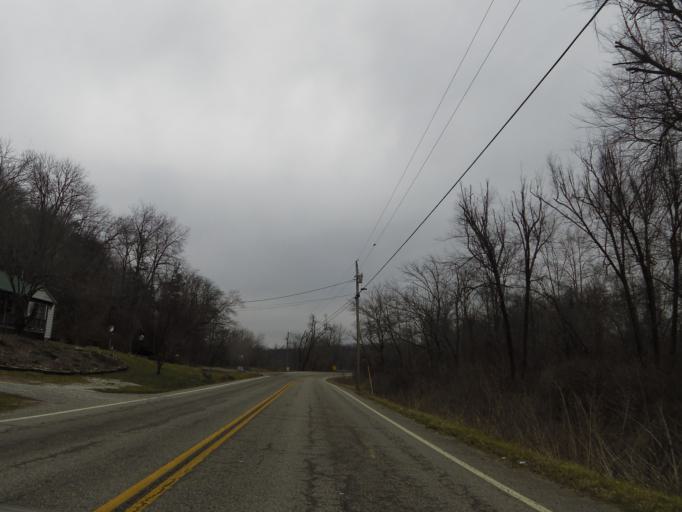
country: US
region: Tennessee
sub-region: Scott County
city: Huntsville
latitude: 36.3131
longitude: -84.6262
